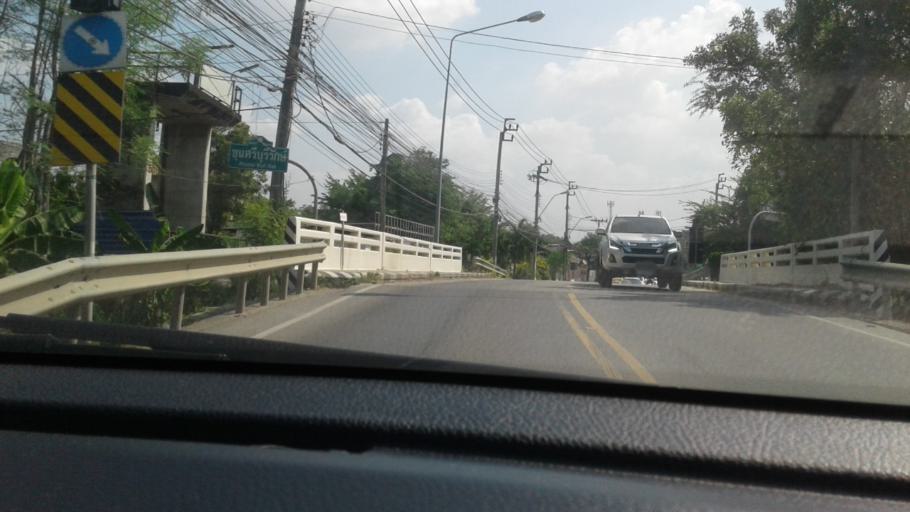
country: TH
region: Bangkok
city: Thawi Watthana
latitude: 13.7988
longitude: 100.3690
